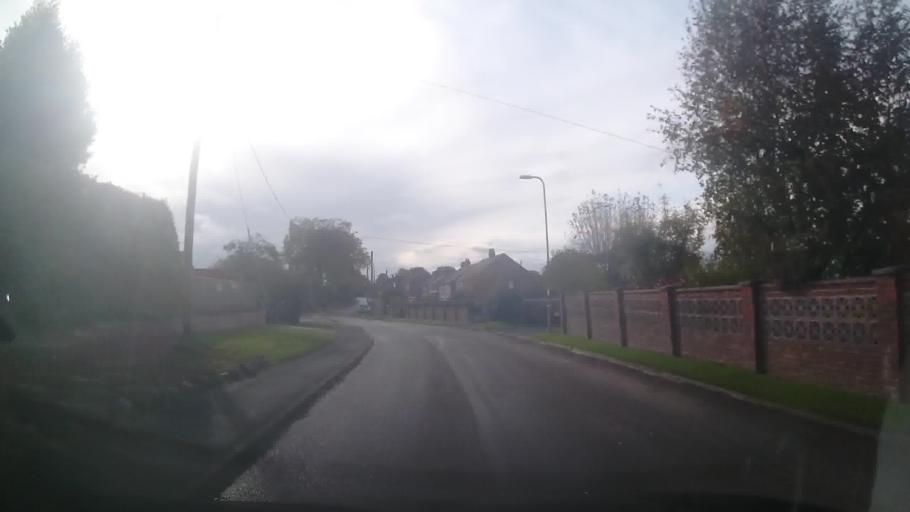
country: GB
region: England
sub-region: Shropshire
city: Whitchurch
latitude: 52.9613
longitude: -2.6910
